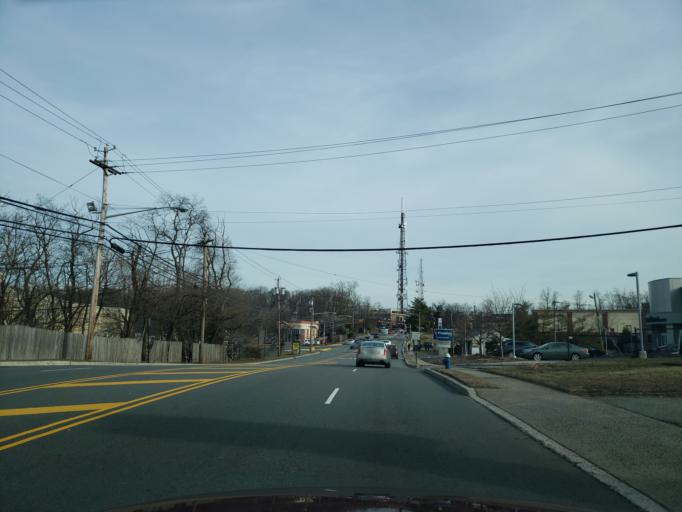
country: US
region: New Jersey
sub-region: Essex County
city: West Orange
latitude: 40.8040
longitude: -74.2502
